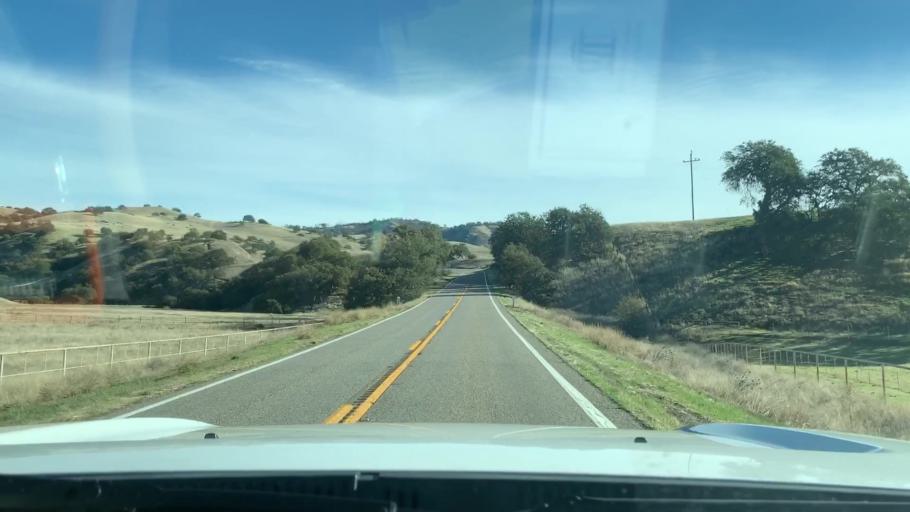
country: US
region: California
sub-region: Monterey County
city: King City
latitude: 36.1884
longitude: -120.8148
